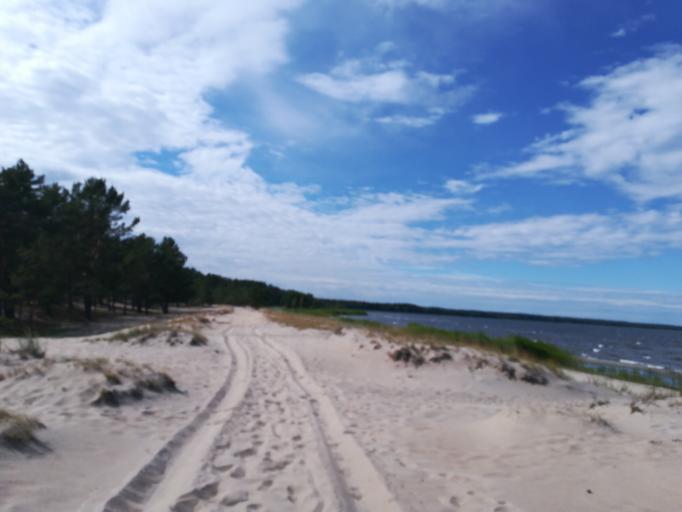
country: RU
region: Leningrad
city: Ust'-Luga
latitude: 59.6801
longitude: 28.2355
